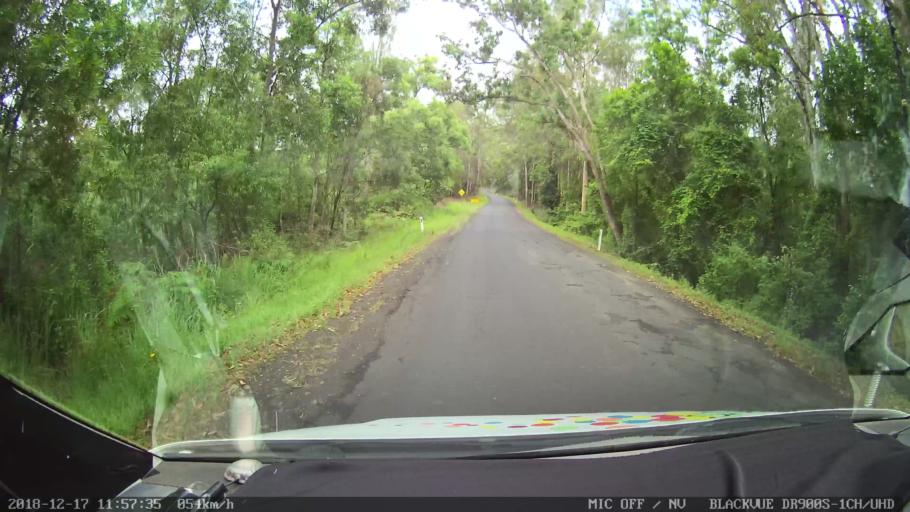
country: AU
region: New South Wales
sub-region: Kyogle
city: Kyogle
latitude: -28.5399
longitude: 152.5725
